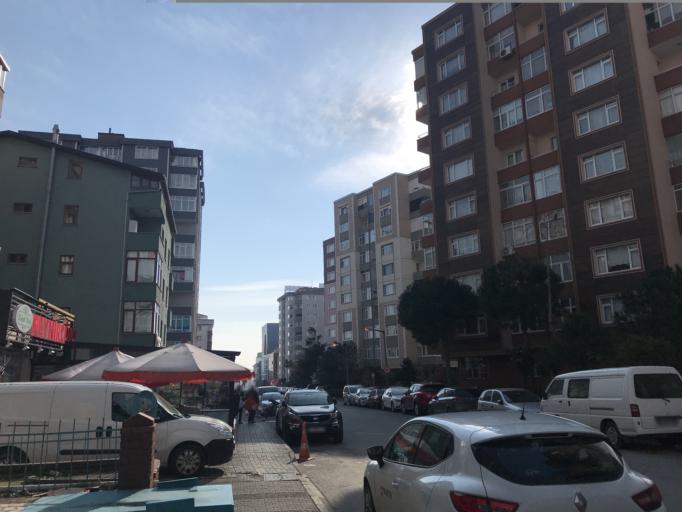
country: TR
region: Istanbul
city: Maltepe
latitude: 40.9397
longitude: 29.1395
